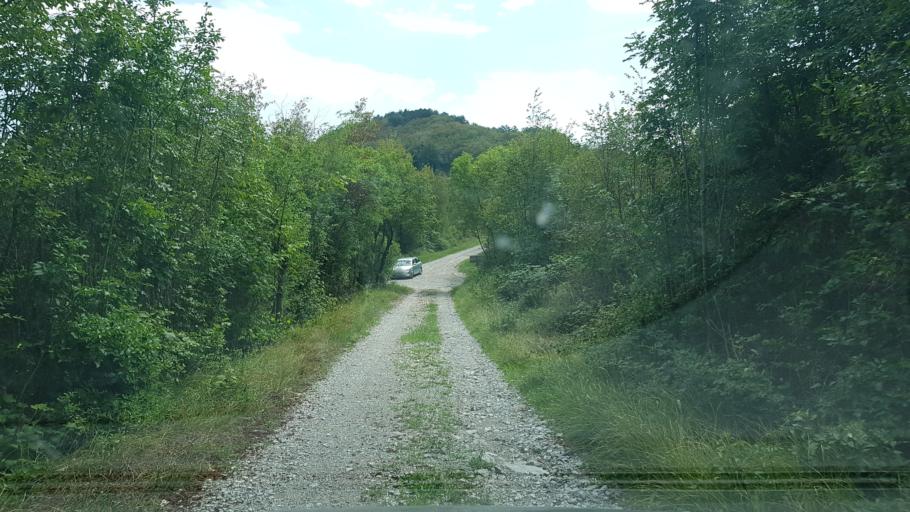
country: SI
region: Nova Gorica
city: Solkan
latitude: 46.0090
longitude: 13.6429
